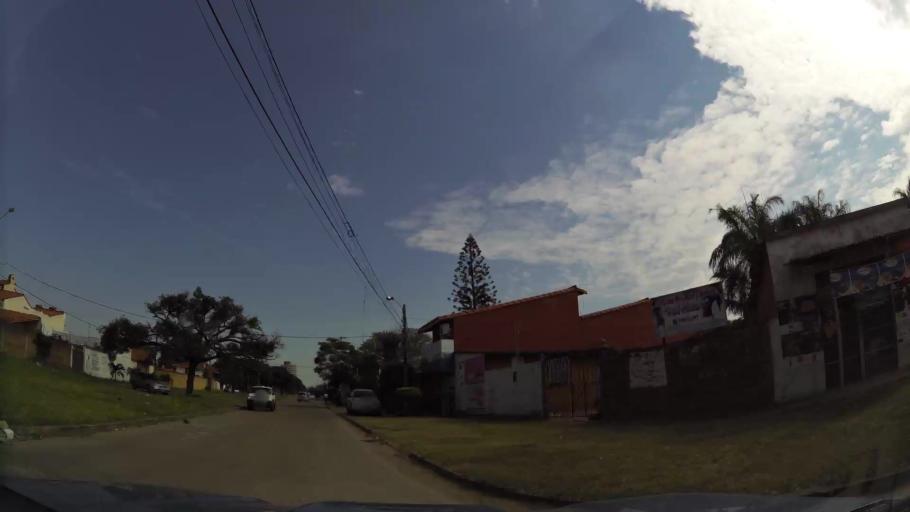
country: BO
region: Santa Cruz
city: Santa Cruz de la Sierra
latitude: -17.7487
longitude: -63.1564
